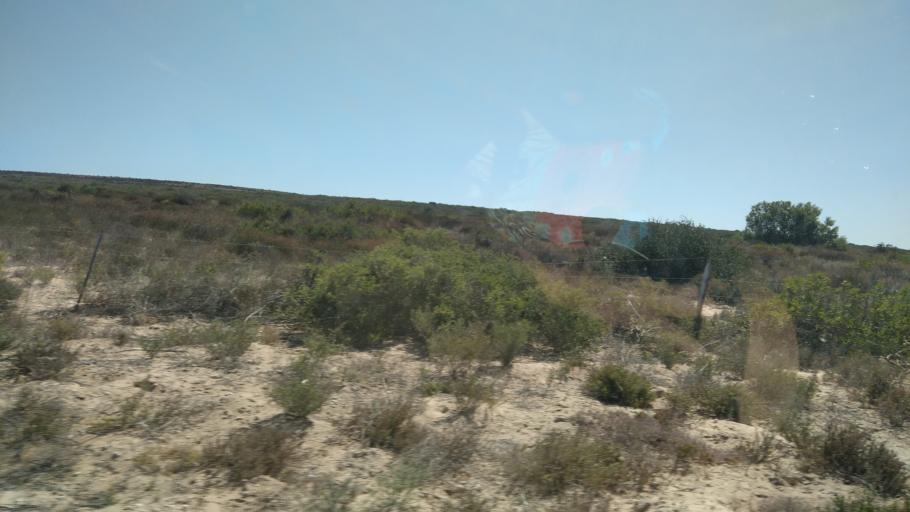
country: ZA
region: Western Cape
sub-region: West Coast District Municipality
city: Vredenburg
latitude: -33.0059
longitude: 18.1220
